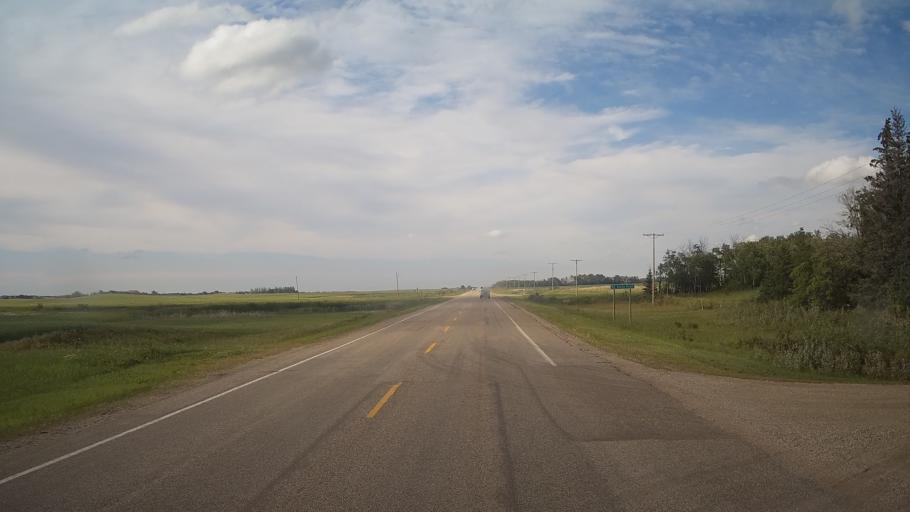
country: CA
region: Saskatchewan
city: Foam Lake
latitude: 51.6062
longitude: -103.8458
